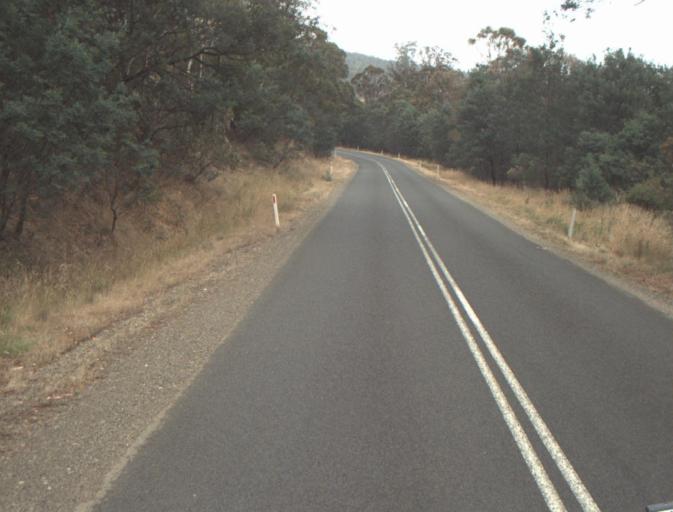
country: AU
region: Tasmania
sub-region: Northern Midlands
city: Evandale
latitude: -41.5037
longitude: 147.3804
